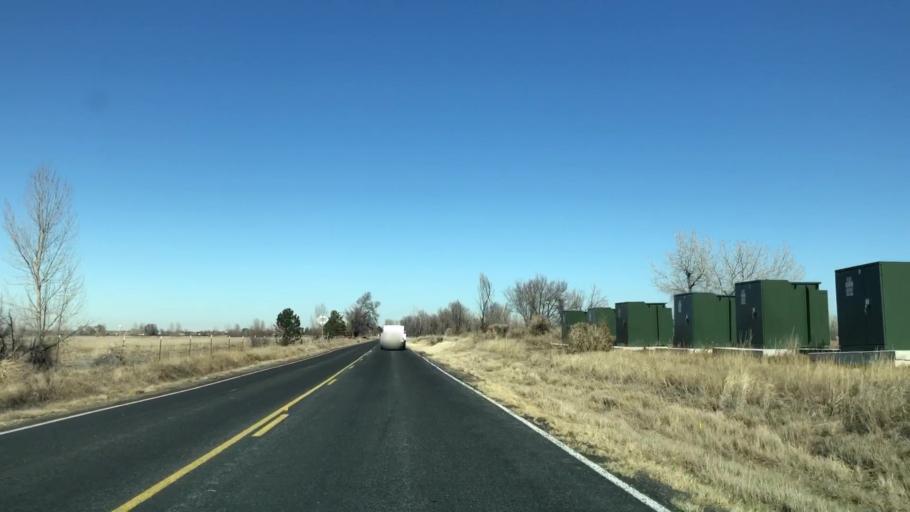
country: US
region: Colorado
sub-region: Weld County
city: Windsor
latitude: 40.4803
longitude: -104.9441
